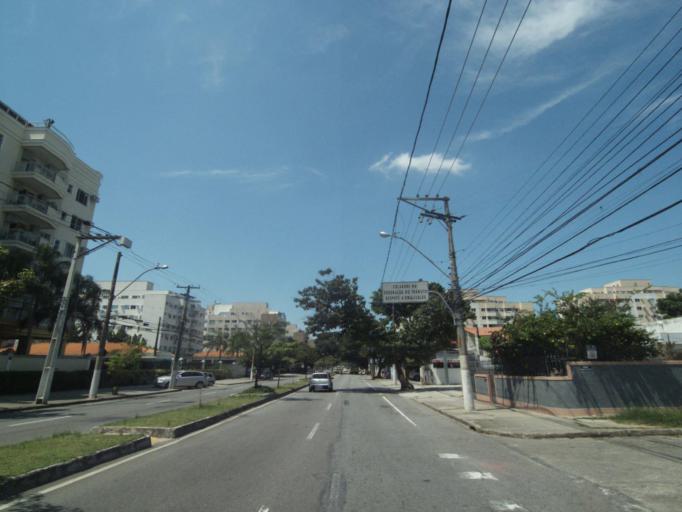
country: BR
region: Rio de Janeiro
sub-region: Niteroi
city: Niteroi
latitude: -22.9072
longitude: -43.0601
